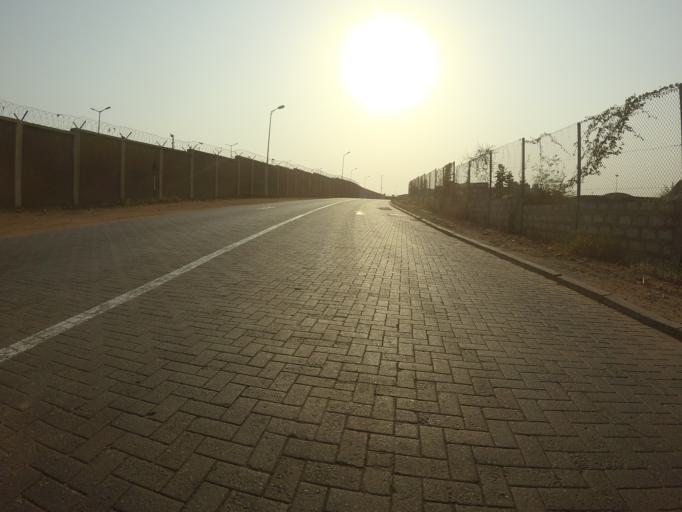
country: GH
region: Greater Accra
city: Tema
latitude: 5.6261
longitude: -0.0032
